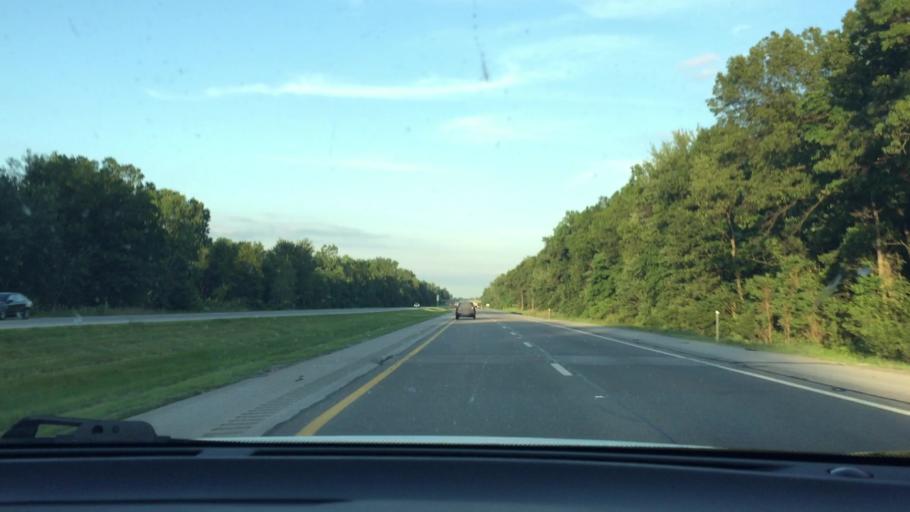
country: US
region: Ohio
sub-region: Lucas County
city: Holland
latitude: 41.5944
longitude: -83.7766
